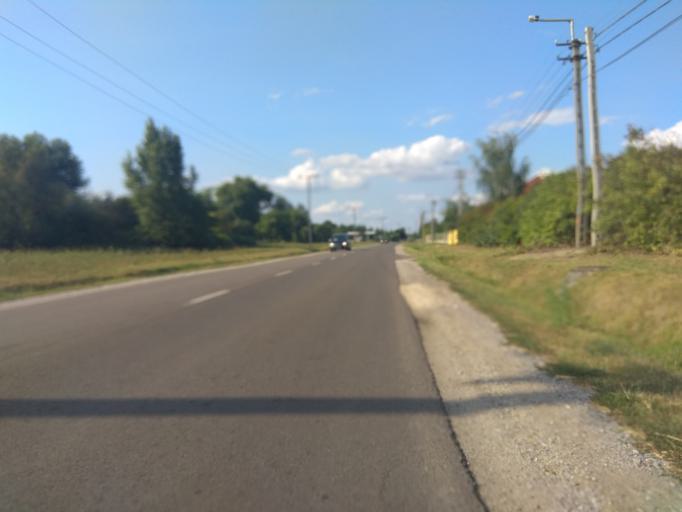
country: HU
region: Borsod-Abauj-Zemplen
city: Mezocsat
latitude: 47.8326
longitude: 20.9005
